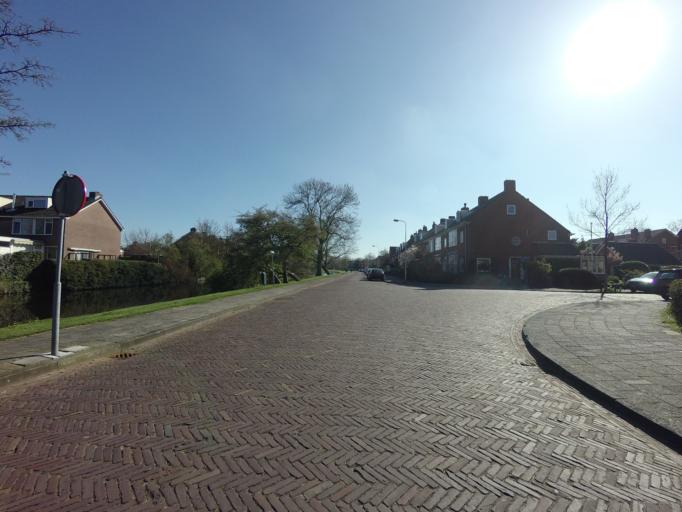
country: NL
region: North Holland
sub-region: Gemeente Heemstede
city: Heemstede
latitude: 52.3559
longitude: 4.6289
